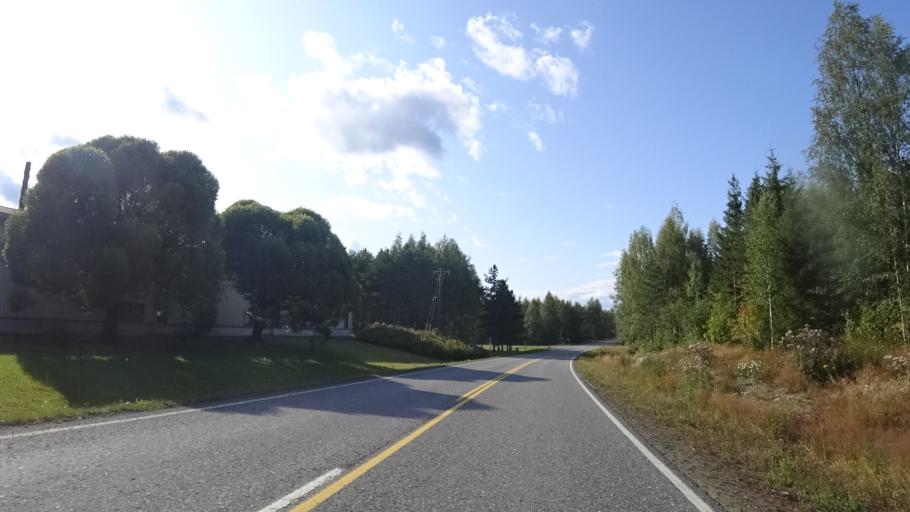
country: FI
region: North Karelia
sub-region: Keski-Karjala
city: Kitee
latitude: 62.0906
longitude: 30.1208
